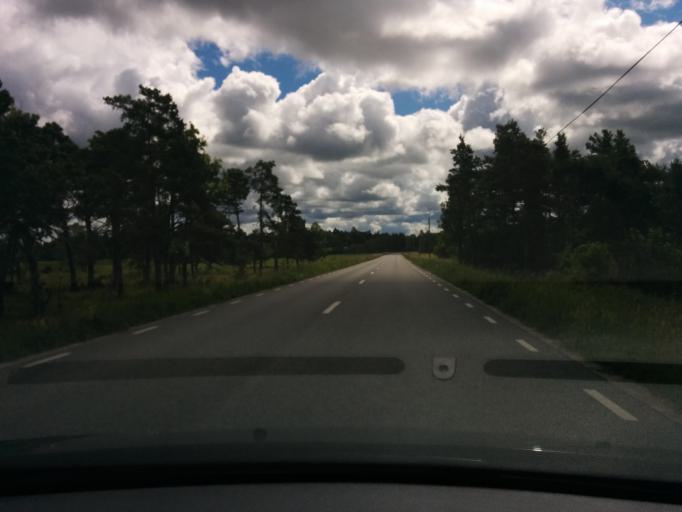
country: SE
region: Gotland
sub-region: Gotland
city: Visby
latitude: 57.6372
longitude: 18.5245
